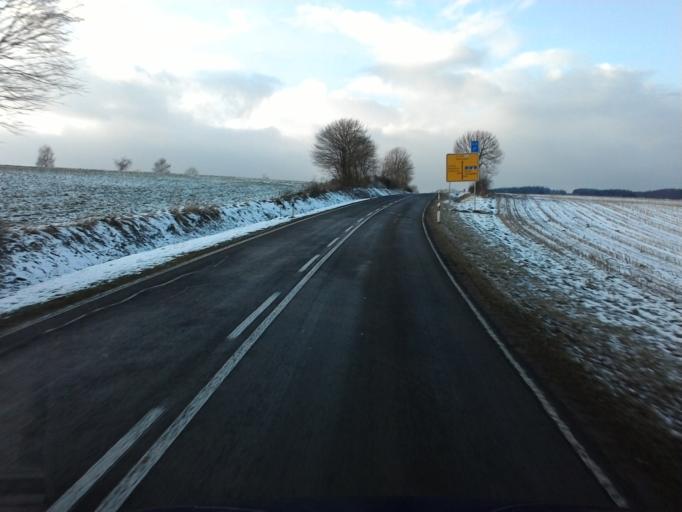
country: DE
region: Rheinland-Pfalz
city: Habscheid
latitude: 50.1931
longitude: 6.2465
